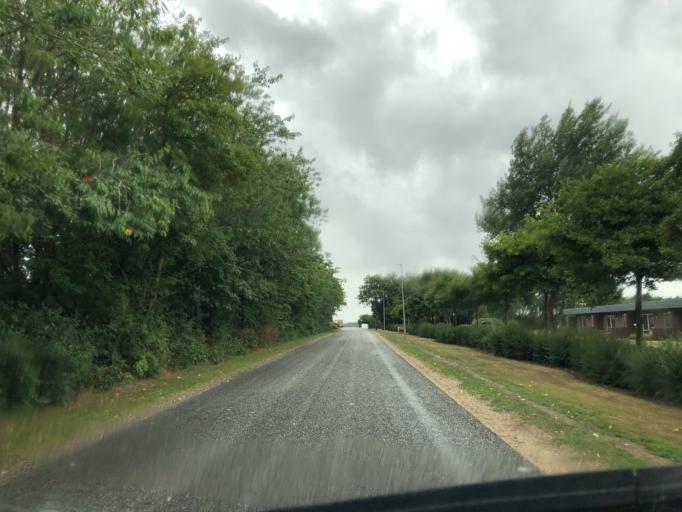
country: DK
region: Central Jutland
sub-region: Ringkobing-Skjern Kommune
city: Videbaek
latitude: 56.1242
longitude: 8.4989
